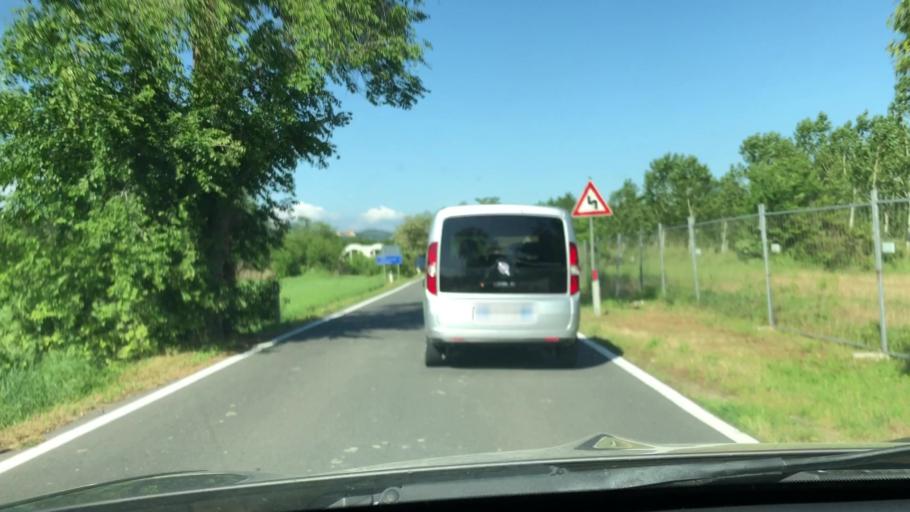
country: IT
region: Tuscany
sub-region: Province of Pisa
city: Capannoli
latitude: 43.5908
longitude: 10.6825
